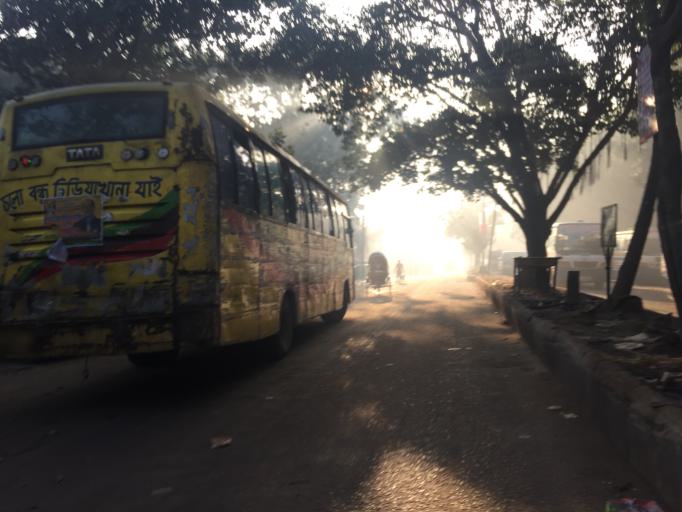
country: BD
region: Dhaka
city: Azimpur
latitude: 23.8114
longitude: 90.3485
